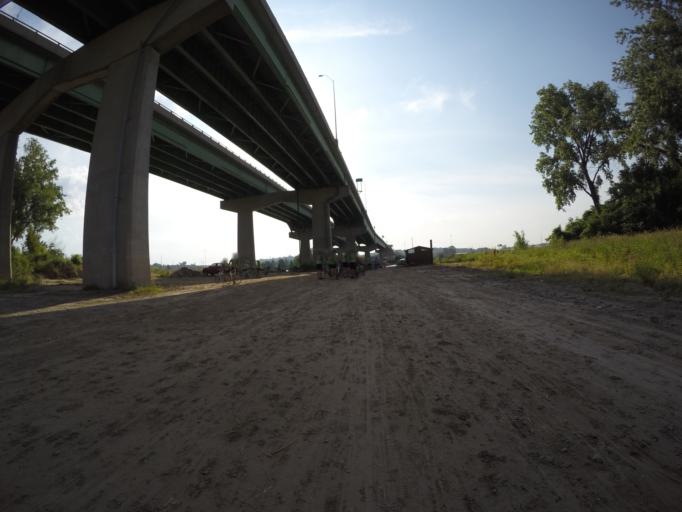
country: US
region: Kansas
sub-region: Doniphan County
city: Elwood
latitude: 39.7489
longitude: -94.8622
